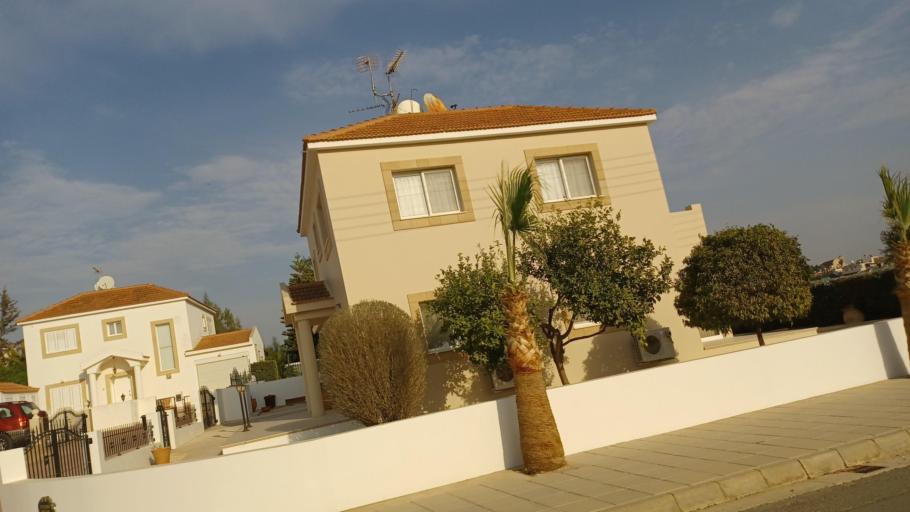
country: CY
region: Ammochostos
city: Acheritou
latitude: 35.0744
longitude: 33.8752
